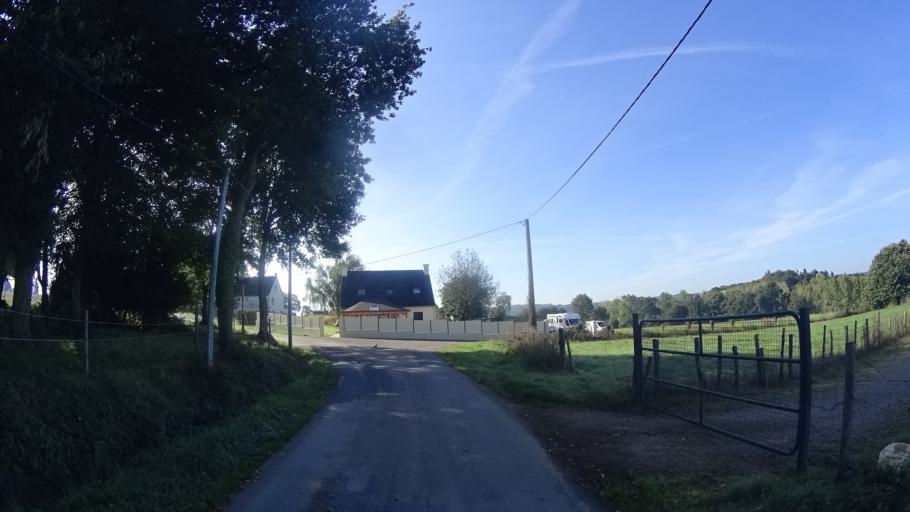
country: FR
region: Brittany
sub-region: Departement du Morbihan
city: Peillac
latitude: 47.7431
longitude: -2.2171
